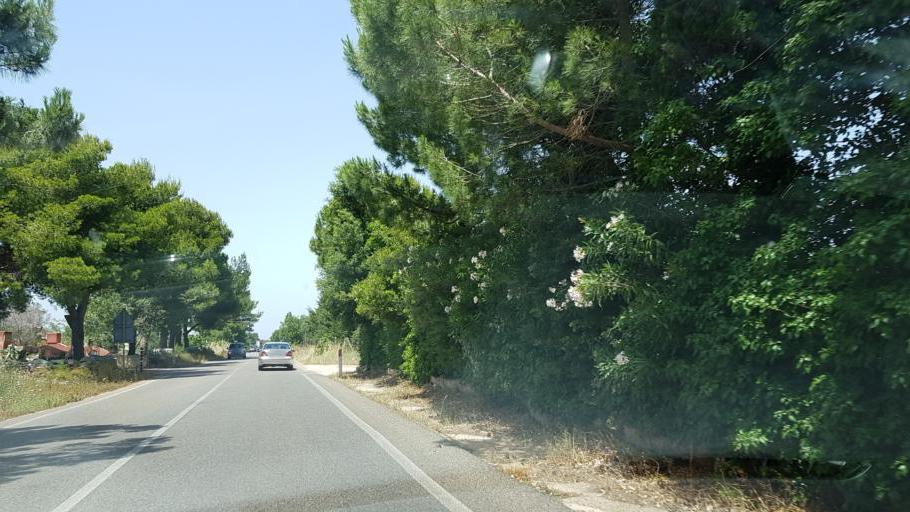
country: IT
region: Apulia
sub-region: Provincia di Lecce
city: Porto Cesareo
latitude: 40.2705
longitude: 17.9061
